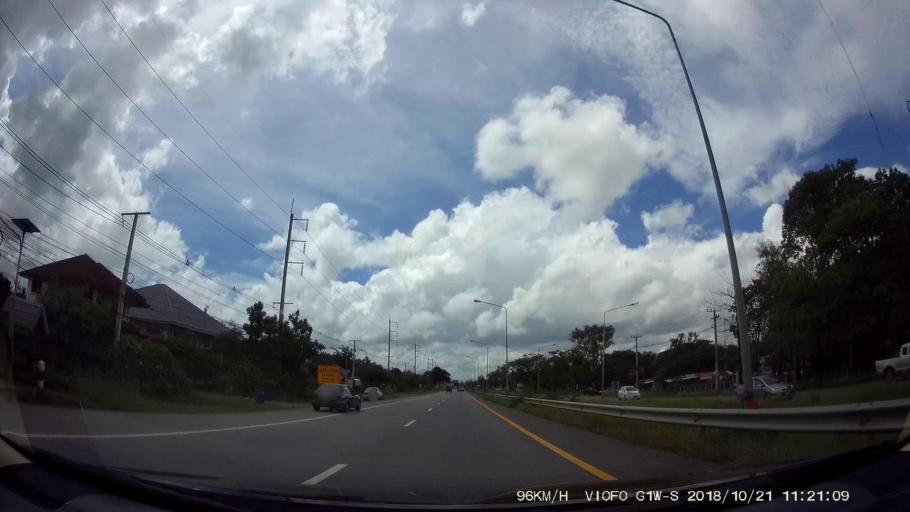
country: TH
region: Chaiyaphum
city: Chaiyaphum
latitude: 15.8496
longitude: 102.0679
